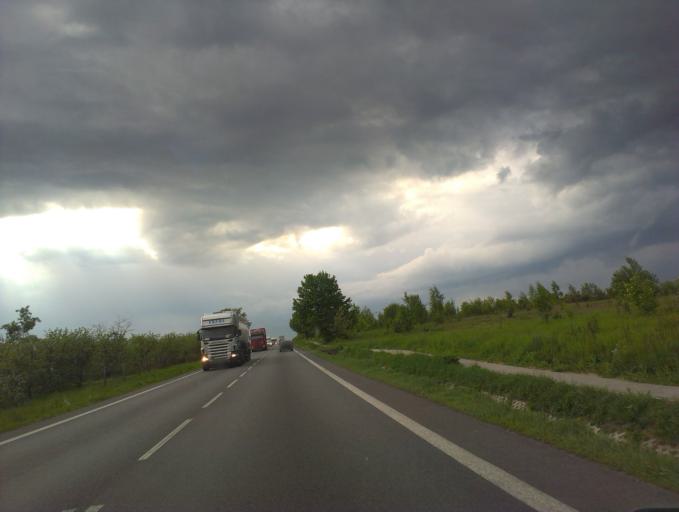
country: PL
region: Masovian Voivodeship
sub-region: Powiat grojecki
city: Pniewy
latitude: 51.9001
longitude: 20.7707
